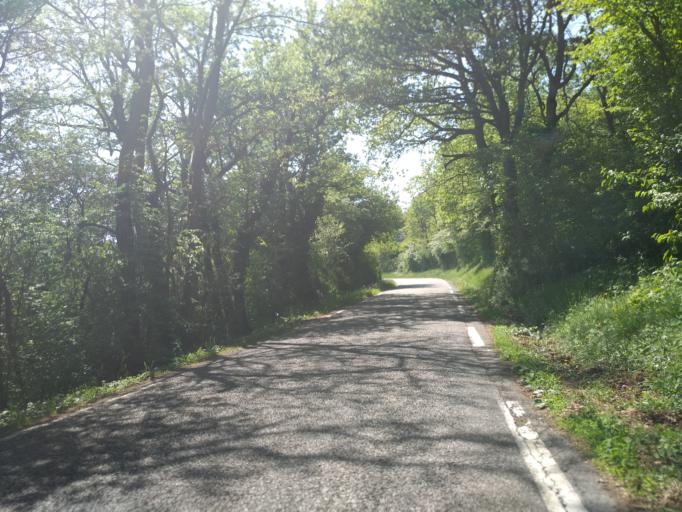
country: FR
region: Rhone-Alpes
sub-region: Departement du Rhone
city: Limonest
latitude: 45.8386
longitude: 4.8010
